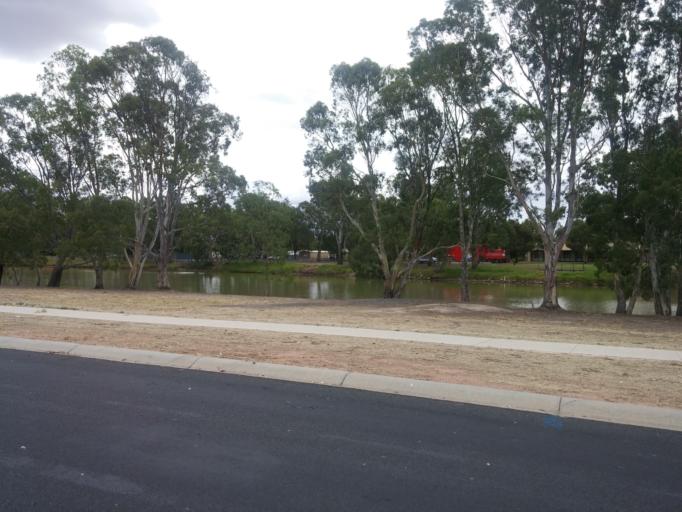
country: AU
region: Victoria
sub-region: Horsham
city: Horsham
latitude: -36.7240
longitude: 142.2017
